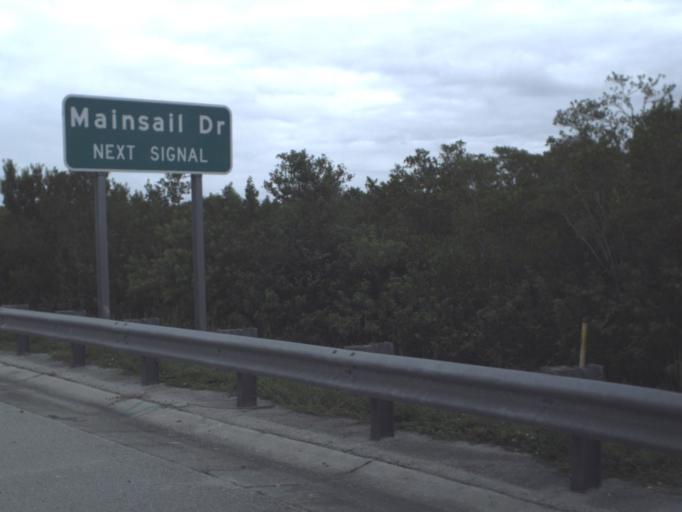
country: US
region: Florida
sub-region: Collier County
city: Marco
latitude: 25.9956
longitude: -81.7018
